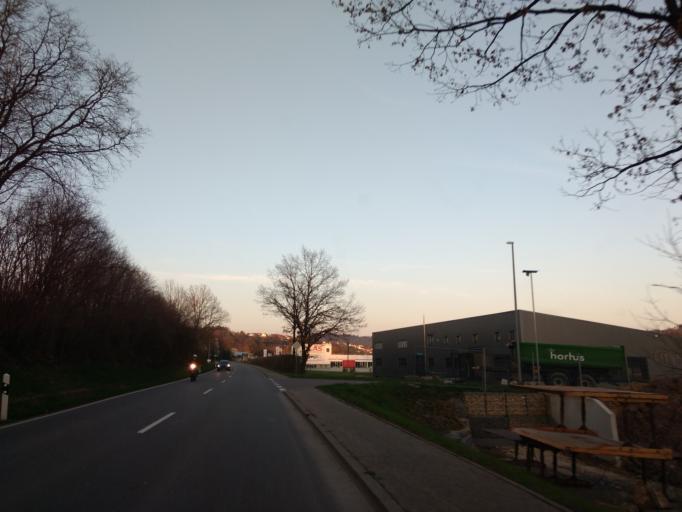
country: DE
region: Baden-Wuerttemberg
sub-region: Regierungsbezirk Stuttgart
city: Lorch
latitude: 48.7958
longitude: 9.6536
